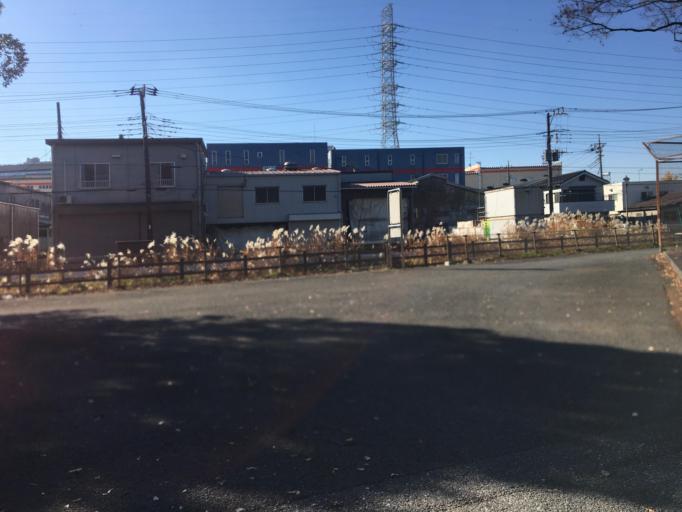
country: JP
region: Saitama
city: Yashio-shi
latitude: 35.8446
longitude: 139.8324
